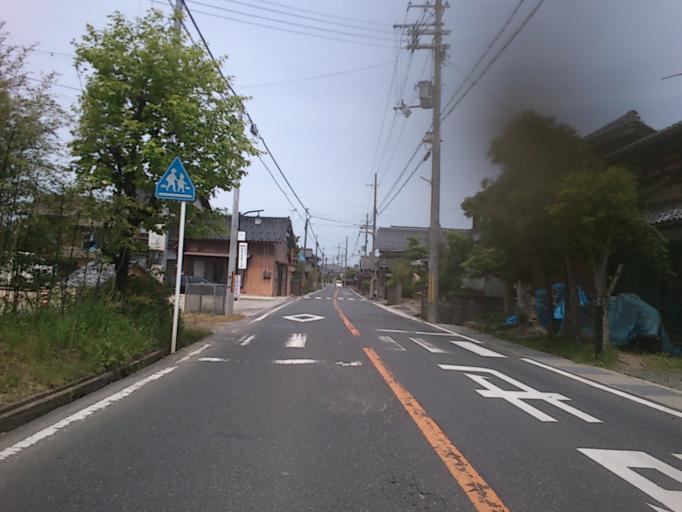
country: JP
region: Kyoto
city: Miyazu
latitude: 35.5992
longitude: 135.0935
